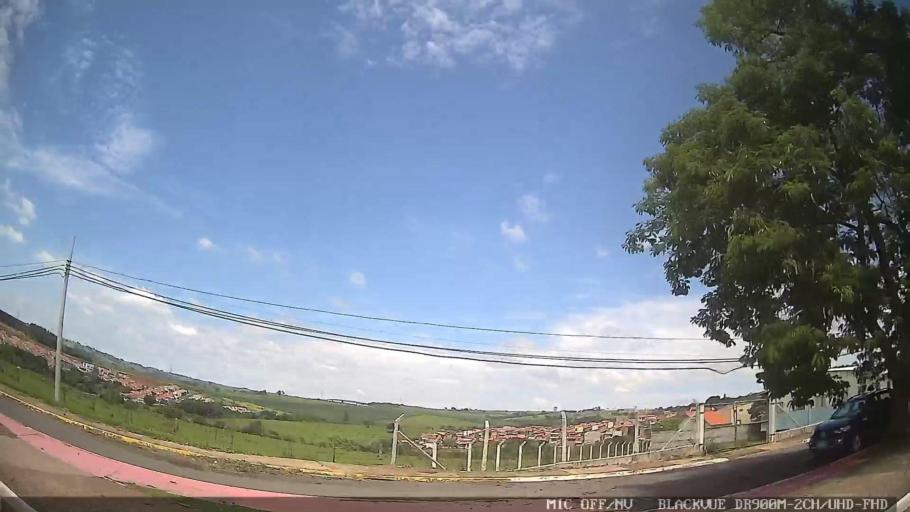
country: BR
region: Sao Paulo
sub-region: Laranjal Paulista
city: Laranjal Paulista
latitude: -23.0635
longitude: -47.8291
